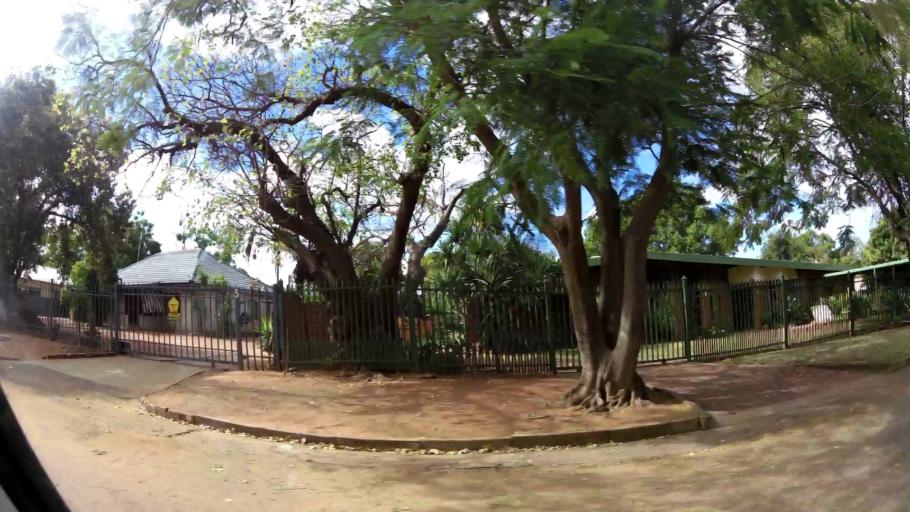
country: ZA
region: Limpopo
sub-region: Waterberg District Municipality
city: Warmbaths
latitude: -24.8875
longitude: 28.2796
